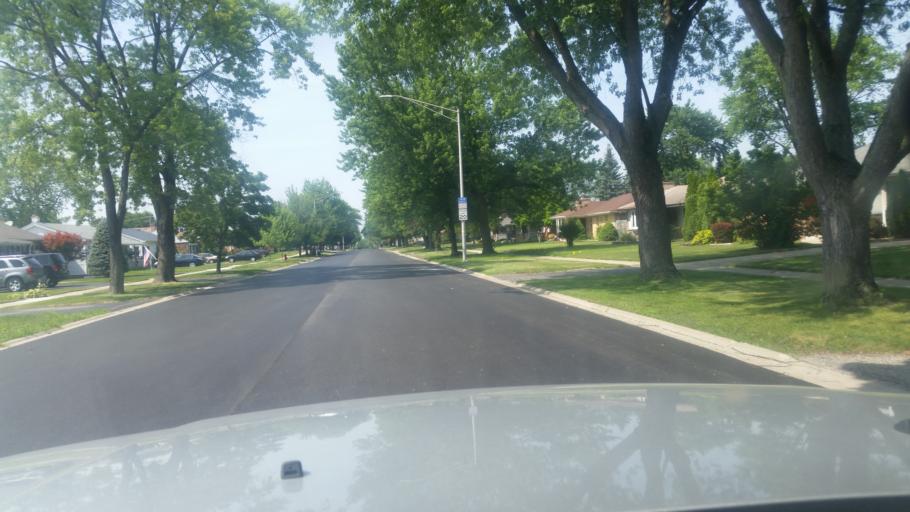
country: US
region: Illinois
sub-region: Cook County
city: Chicago Ridge
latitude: 41.6925
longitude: -87.7691
